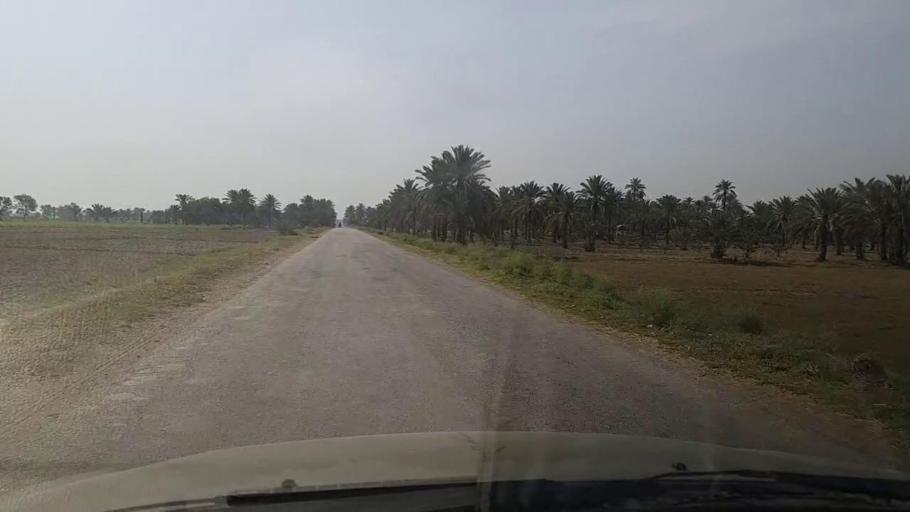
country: PK
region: Sindh
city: Gambat
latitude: 27.4701
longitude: 68.4757
